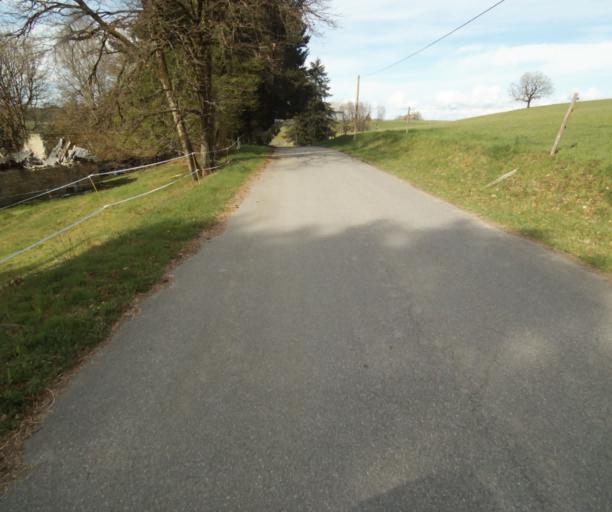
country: FR
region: Limousin
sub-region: Departement de la Correze
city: Correze
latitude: 45.3510
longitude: 1.8706
